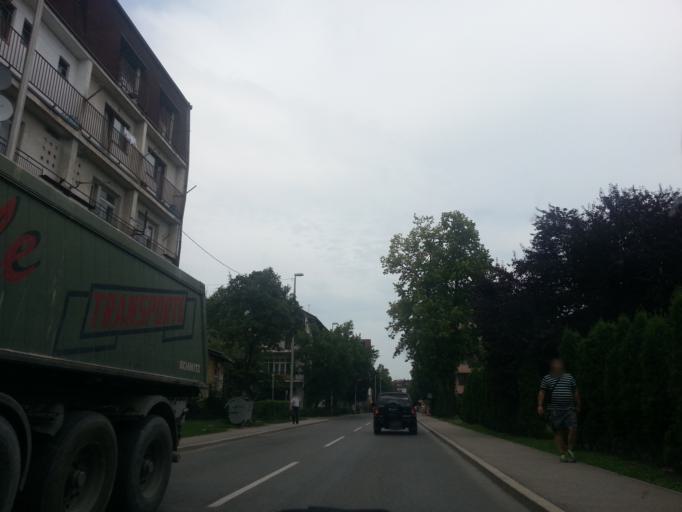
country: BA
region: Brcko
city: Brcko
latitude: 44.8723
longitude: 18.8109
